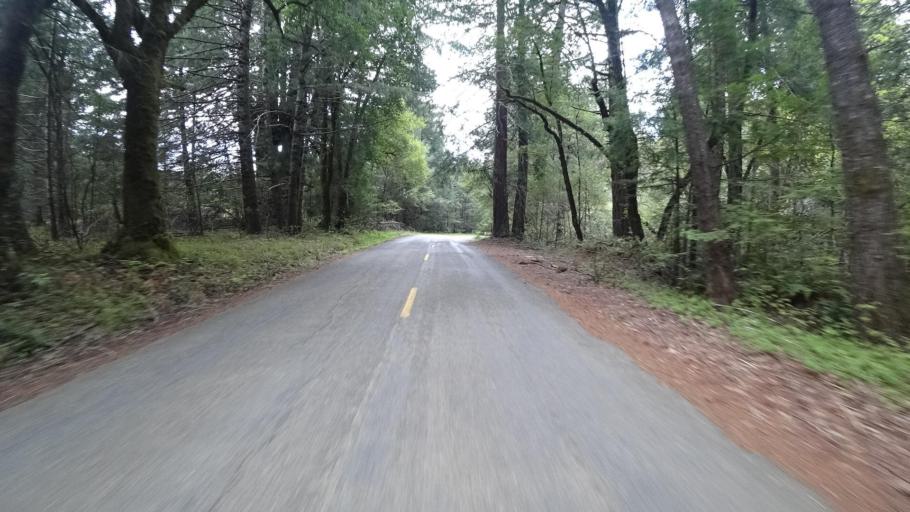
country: US
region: California
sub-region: Humboldt County
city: Redway
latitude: 40.0106
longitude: -123.9302
